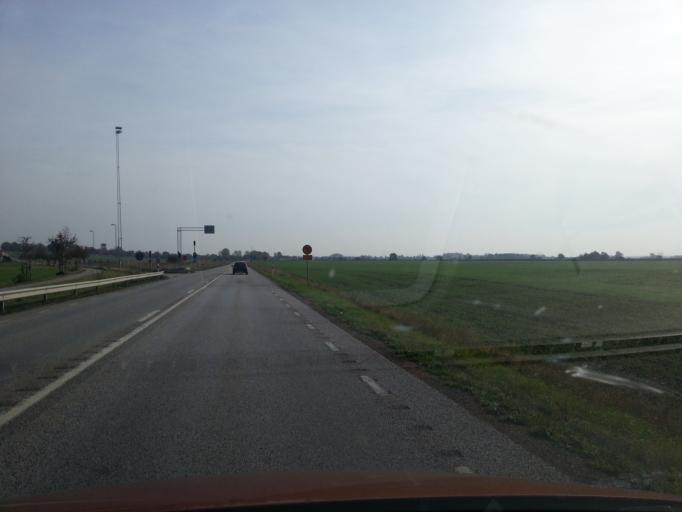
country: SE
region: Skane
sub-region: Lunds Kommun
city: Genarp
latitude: 55.6675
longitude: 13.3210
